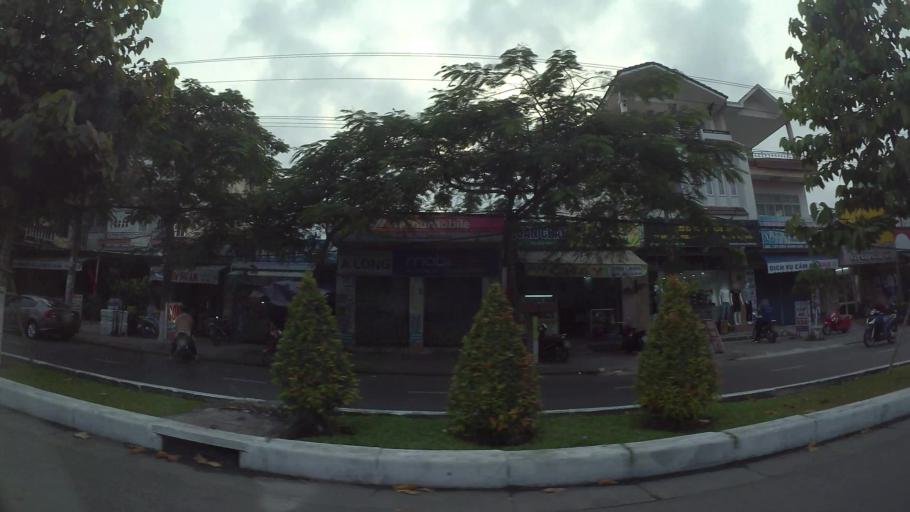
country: VN
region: Da Nang
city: Son Tra
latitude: 16.0488
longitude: 108.2381
